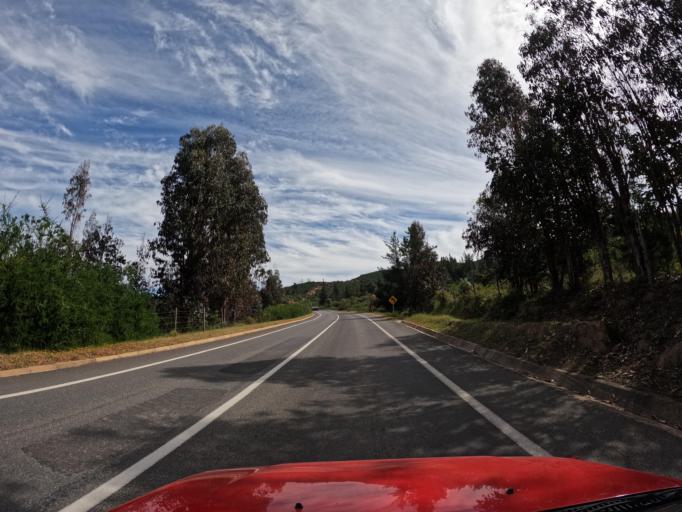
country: CL
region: Maule
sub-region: Provincia de Talca
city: Talca
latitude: -35.1585
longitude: -71.9698
